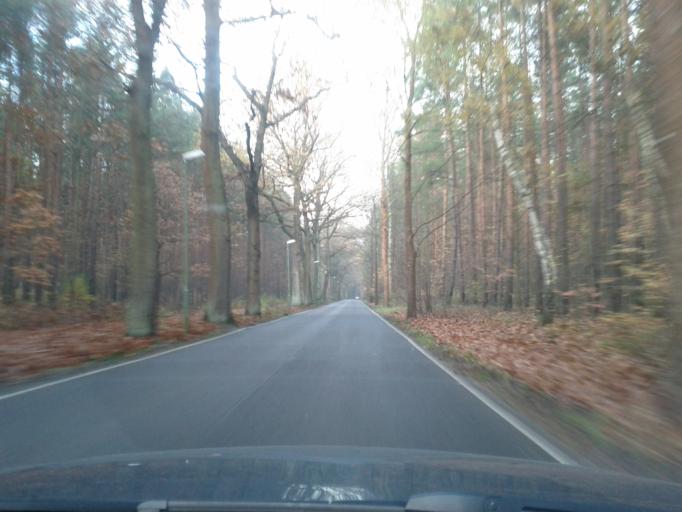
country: DE
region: Brandenburg
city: Schoneiche
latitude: 52.4591
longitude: 13.6936
